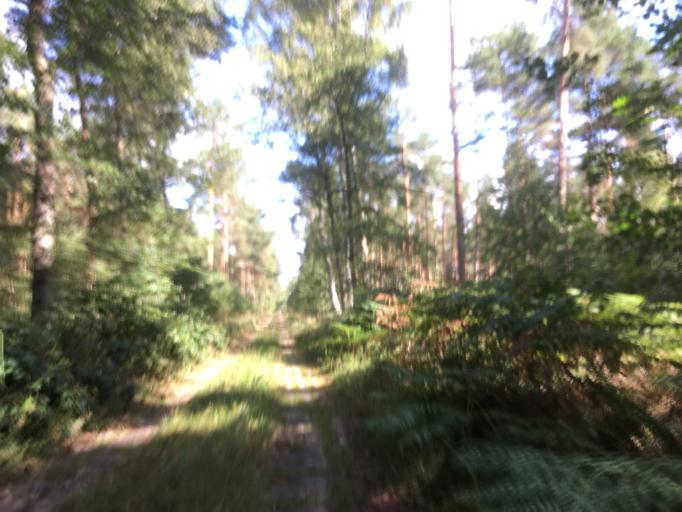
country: DE
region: Brandenburg
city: Halbe
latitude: 52.1667
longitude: 13.7492
